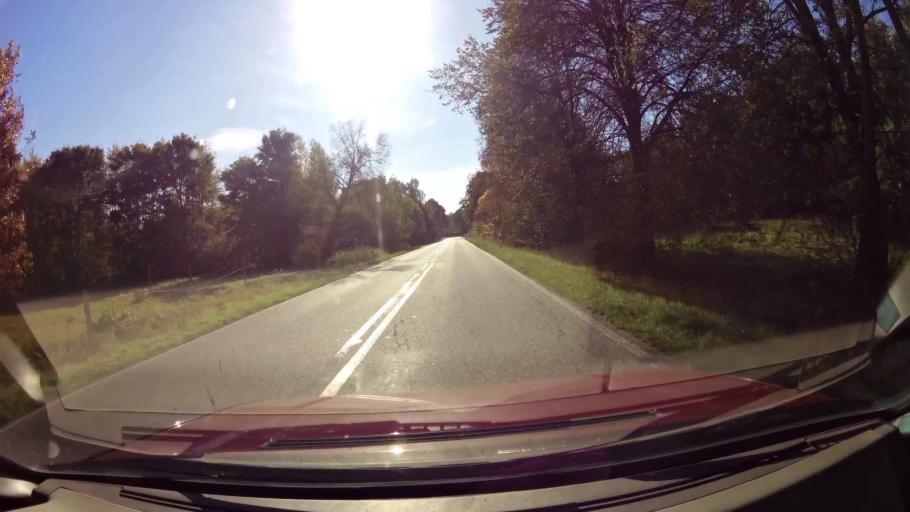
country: PL
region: West Pomeranian Voivodeship
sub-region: Powiat swidwinski
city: Polczyn-Zdroj
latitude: 53.7282
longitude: 16.1055
